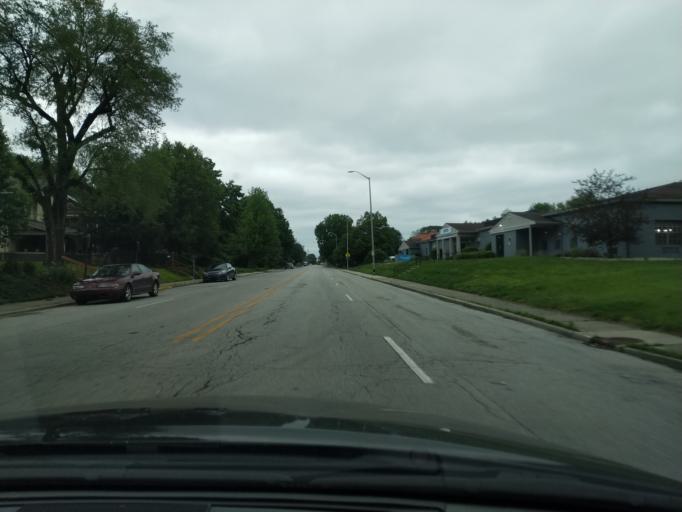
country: US
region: Indiana
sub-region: Marion County
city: Broad Ripple
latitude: 39.8229
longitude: -86.1498
